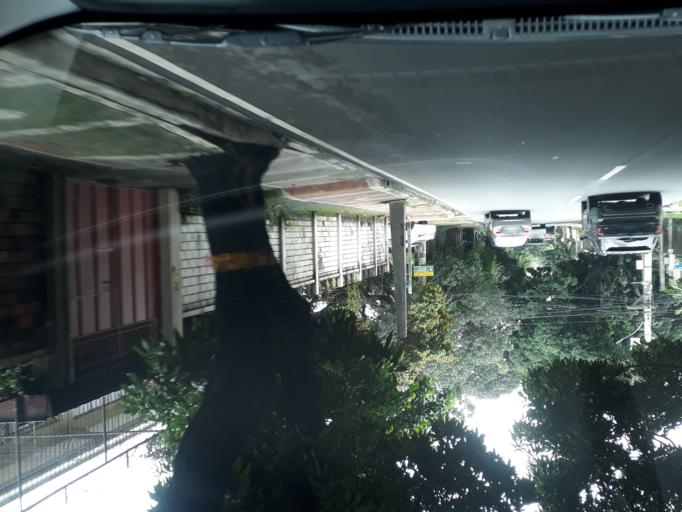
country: PH
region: Metro Manila
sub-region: San Juan
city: San Juan
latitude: 14.6187
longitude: 121.0317
